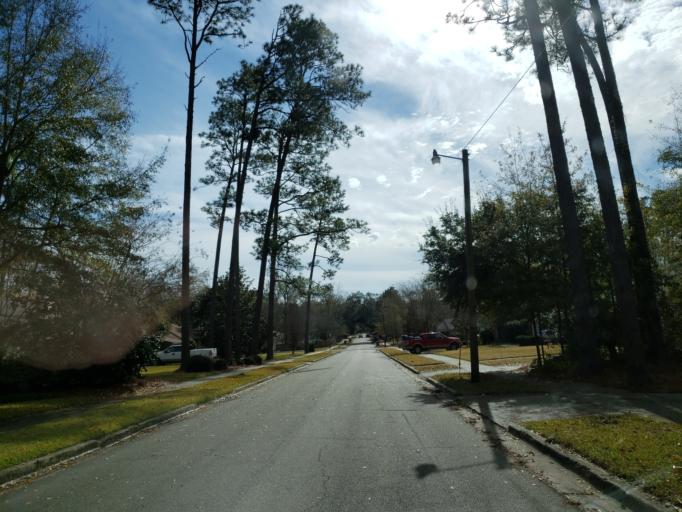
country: US
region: Mississippi
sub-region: Forrest County
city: Hattiesburg
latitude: 31.3202
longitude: -89.3240
